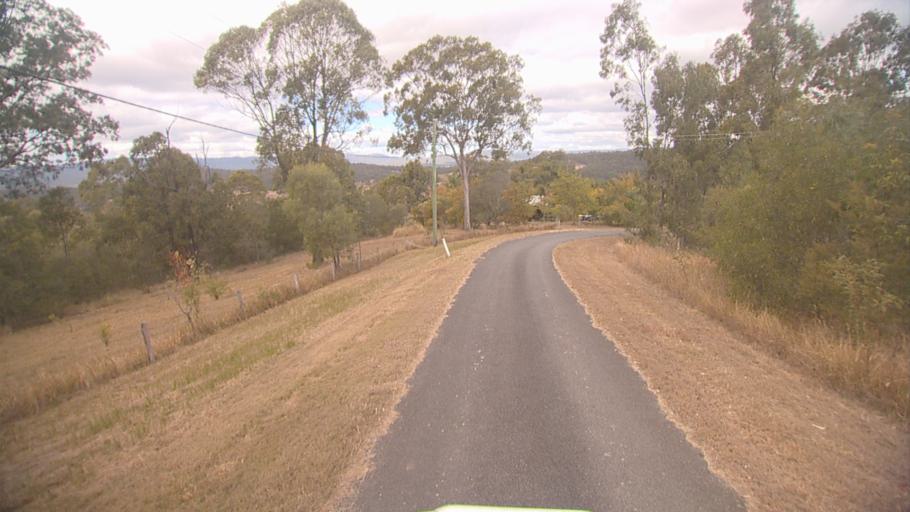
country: AU
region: Queensland
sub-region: Logan
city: Cedar Vale
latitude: -27.9019
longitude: 153.0385
